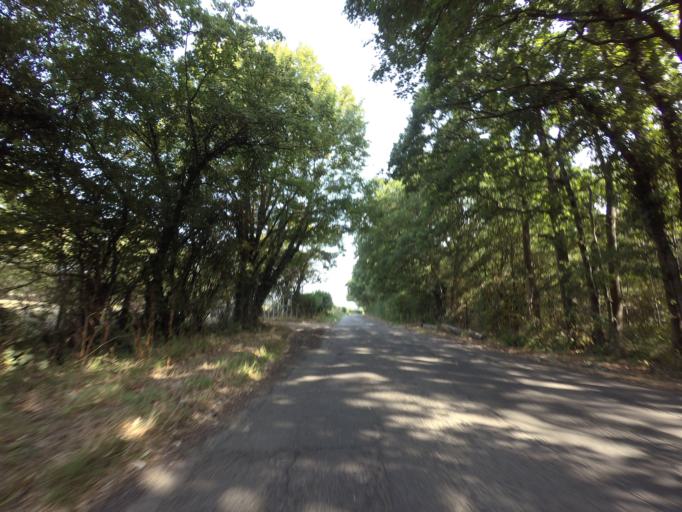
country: GB
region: England
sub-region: Kent
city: Headcorn
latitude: 51.1563
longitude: 0.6052
